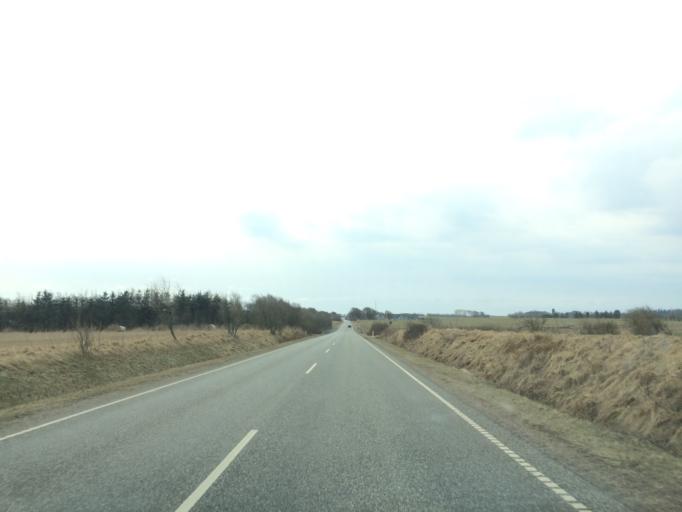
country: DK
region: Central Jutland
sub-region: Ringkobing-Skjern Kommune
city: Skjern
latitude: 56.0683
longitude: 8.5058
